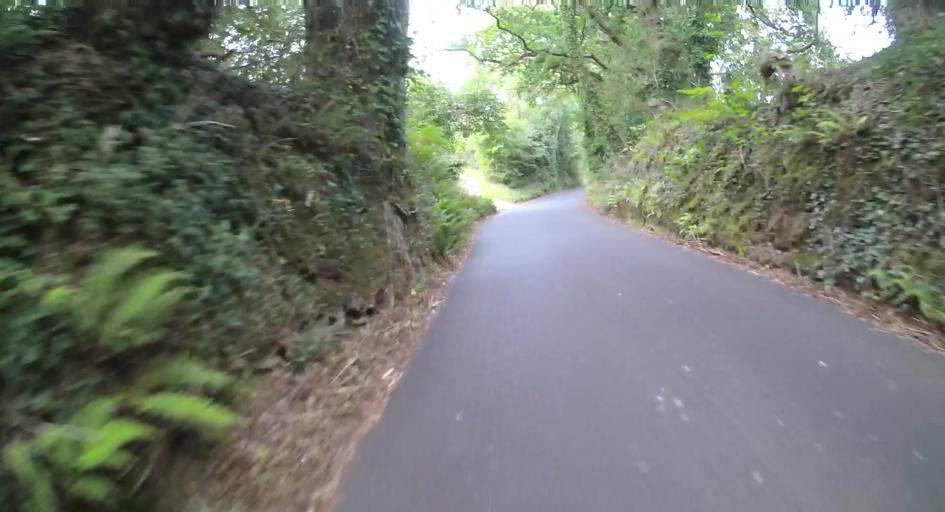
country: GB
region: England
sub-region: Isle of Wight
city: Niton
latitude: 50.6284
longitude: -1.2721
